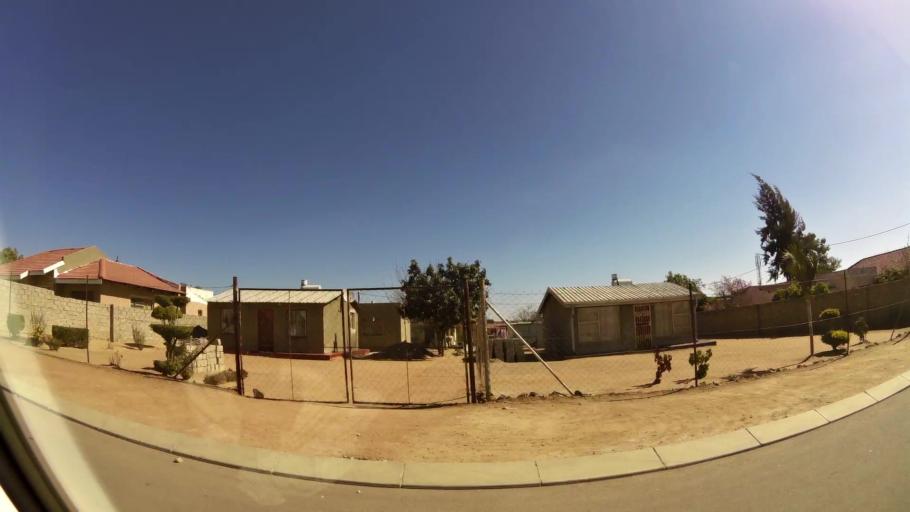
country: ZA
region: Limpopo
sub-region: Capricorn District Municipality
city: Polokwane
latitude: -23.8535
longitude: 29.4089
